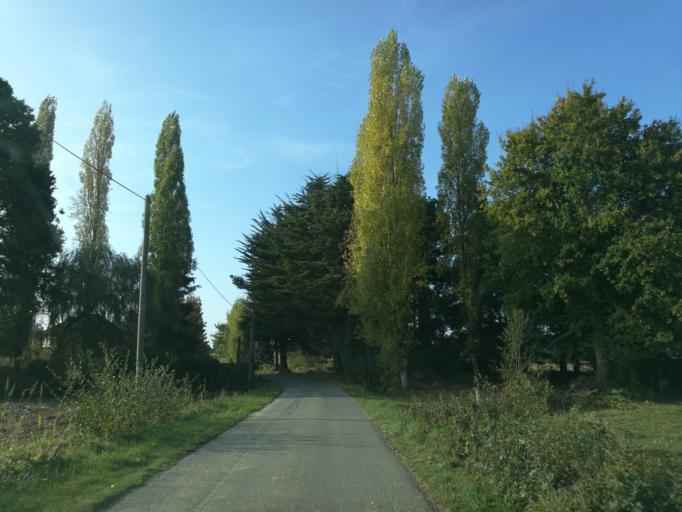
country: FR
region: Brittany
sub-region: Departement d'Ille-et-Vilaine
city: Pleumeleuc
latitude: 48.1674
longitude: -1.9116
